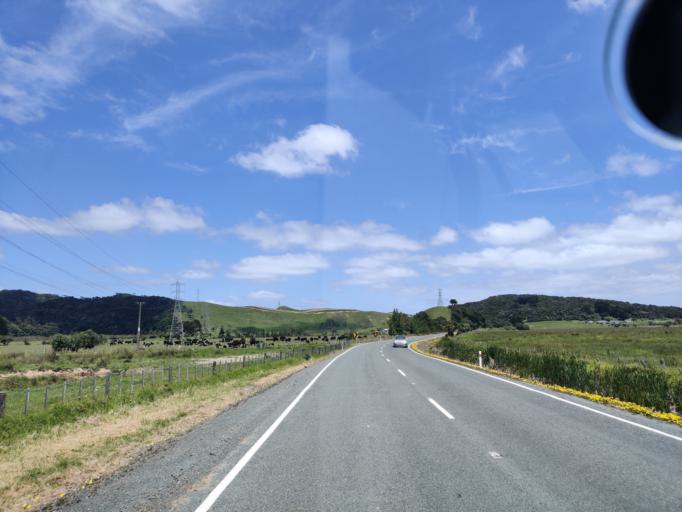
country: NZ
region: Auckland
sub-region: Auckland
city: Wellsford
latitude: -36.4275
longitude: 174.4444
